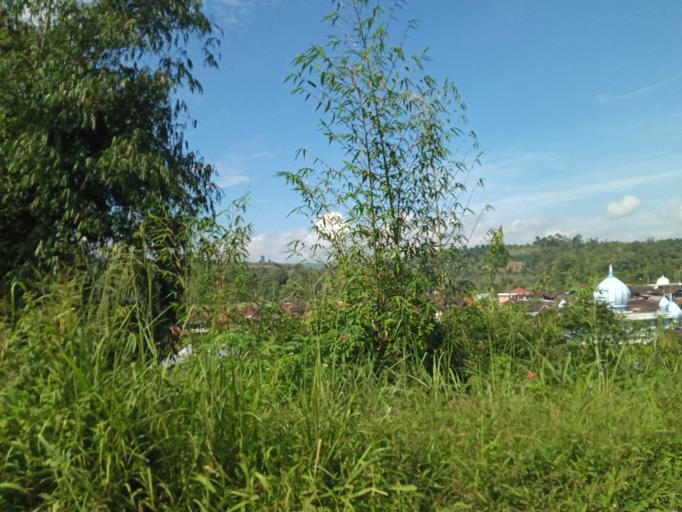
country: ID
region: Jambi
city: Sungai Penuh
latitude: -2.1657
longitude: 101.5949
